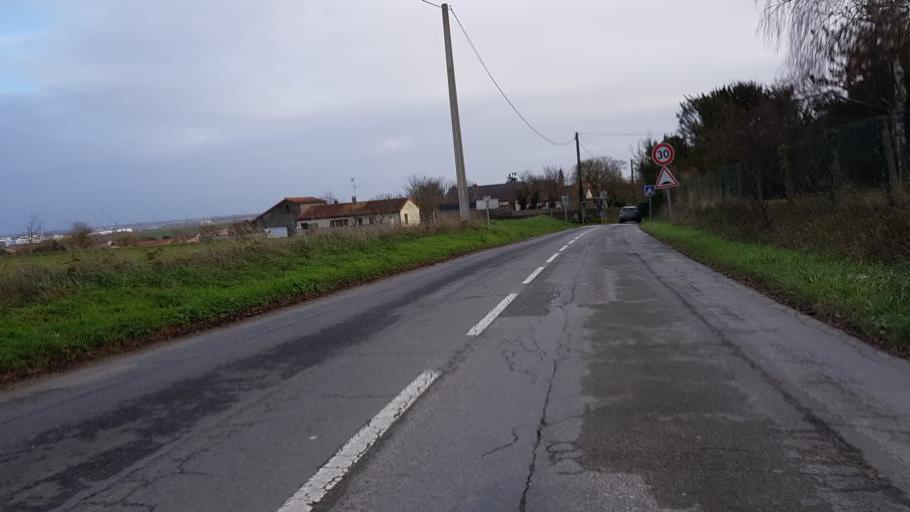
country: FR
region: Poitou-Charentes
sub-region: Departement de la Vienne
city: Avanton
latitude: 46.6599
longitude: 0.3331
